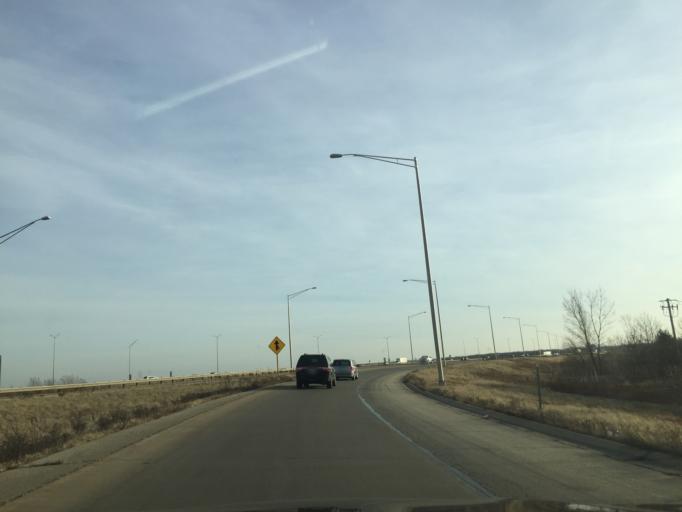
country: US
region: Illinois
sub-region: Will County
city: Bolingbrook
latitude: 41.7007
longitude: -88.0322
